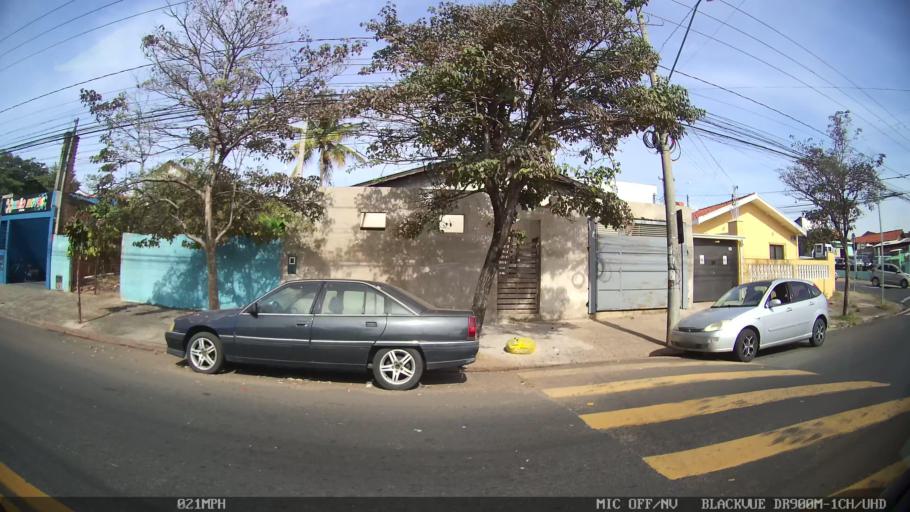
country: BR
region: Sao Paulo
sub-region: Piracicaba
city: Piracicaba
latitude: -22.7446
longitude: -47.6633
